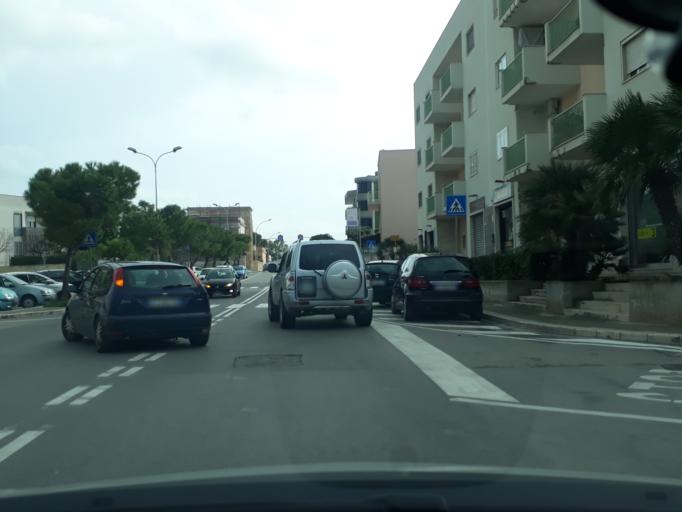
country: IT
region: Apulia
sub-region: Provincia di Bari
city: Monopoli
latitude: 40.9512
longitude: 17.2871
